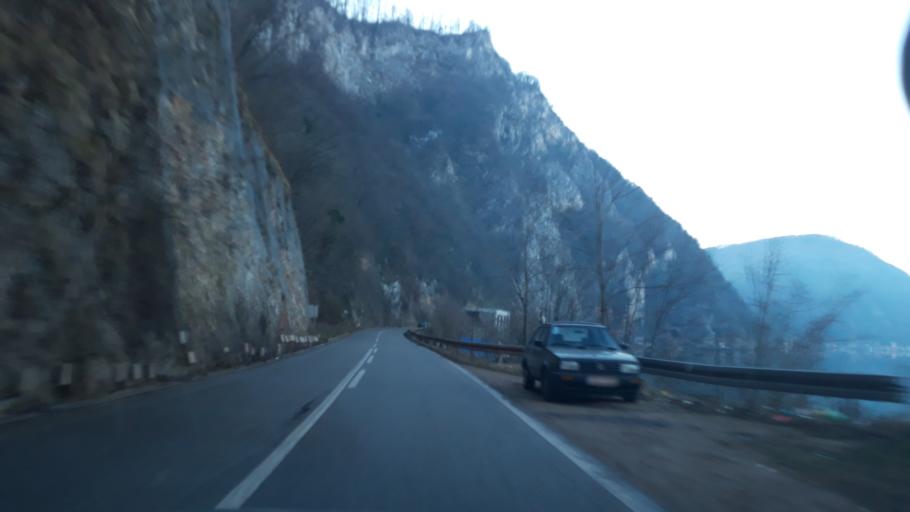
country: RS
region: Central Serbia
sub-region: Macvanski Okrug
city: Mali Zvornik
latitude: 44.3409
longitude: 19.1171
